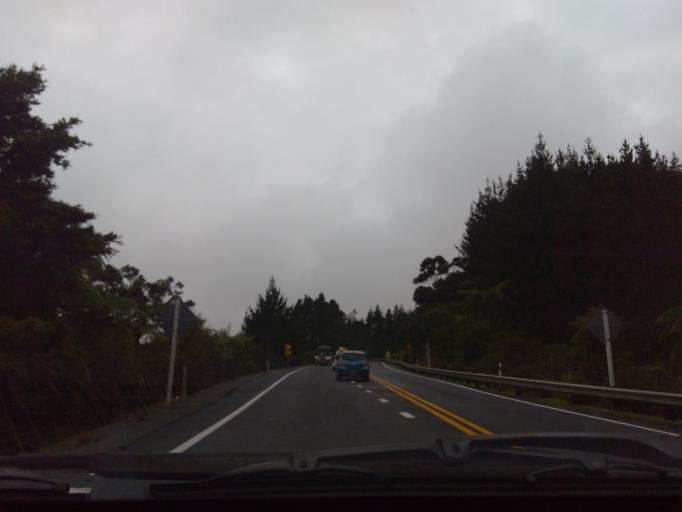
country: NZ
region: Northland
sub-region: Whangarei
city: Ruakaka
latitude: -36.0711
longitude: 174.4196
